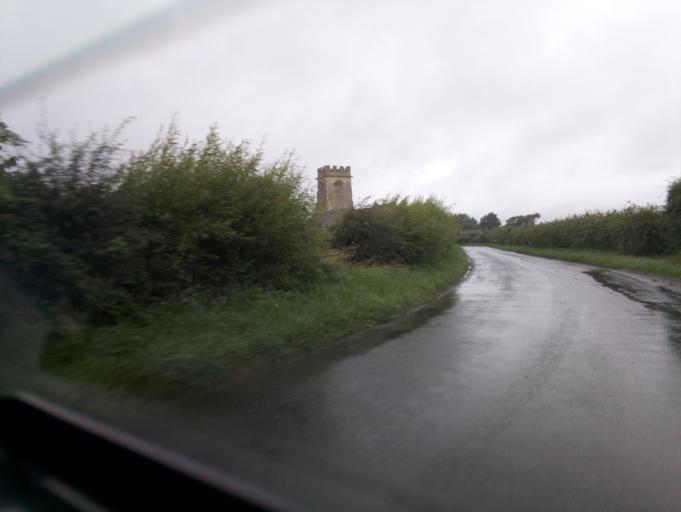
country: GB
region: England
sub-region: Gloucestershire
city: Uckington
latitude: 51.9325
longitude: -2.1160
